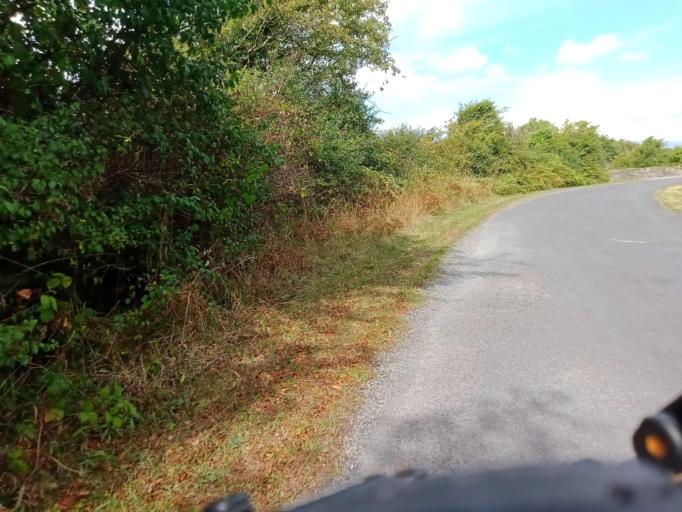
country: IE
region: Munster
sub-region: Waterford
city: Dungarvan
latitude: 52.1117
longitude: -7.5089
